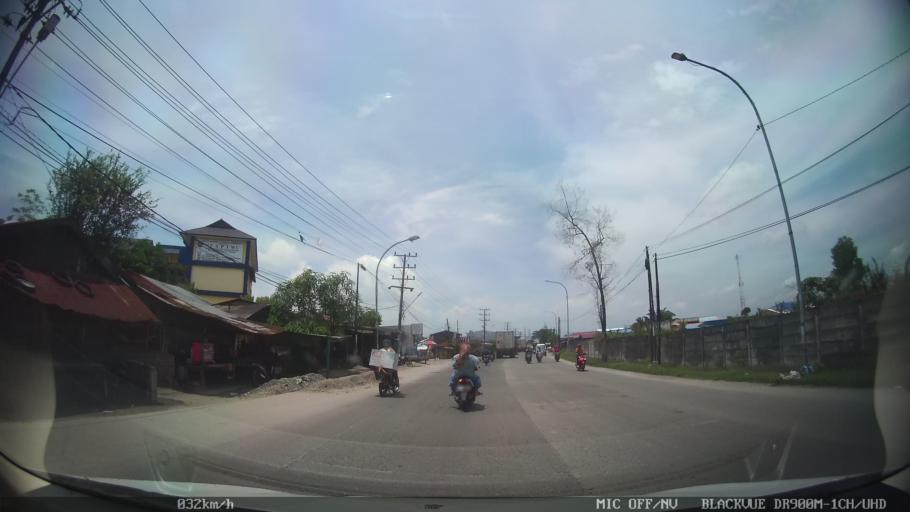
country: ID
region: North Sumatra
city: Belawan
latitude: 3.7600
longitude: 98.6804
